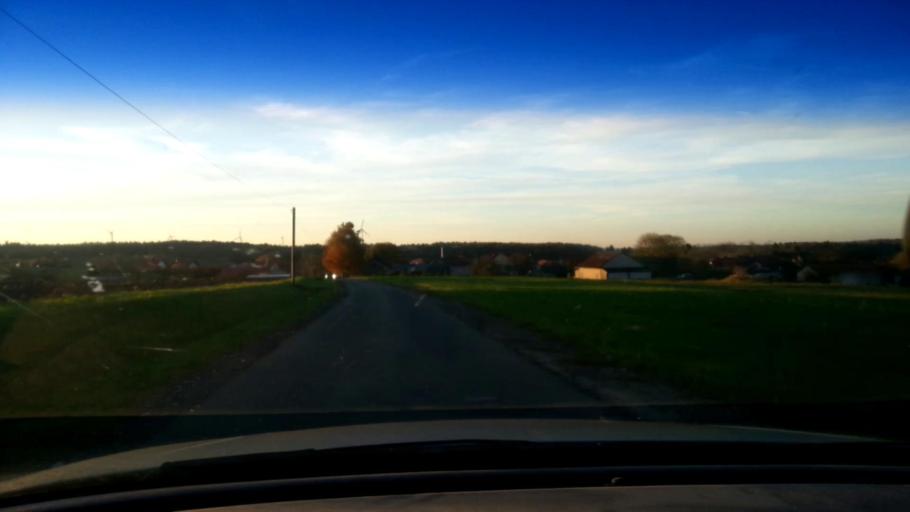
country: DE
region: Bavaria
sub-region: Upper Franconia
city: Heiligenstadt
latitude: 49.8442
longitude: 11.1224
